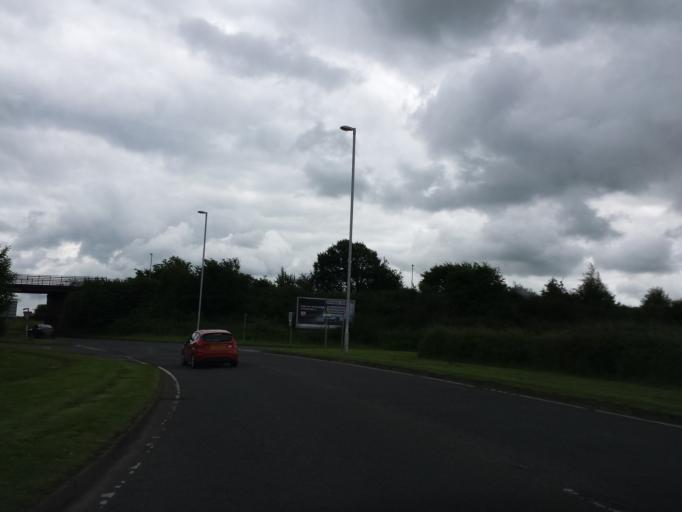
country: GB
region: Scotland
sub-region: Dumfries and Galloway
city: Dumfries
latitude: 55.0648
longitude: -3.6465
